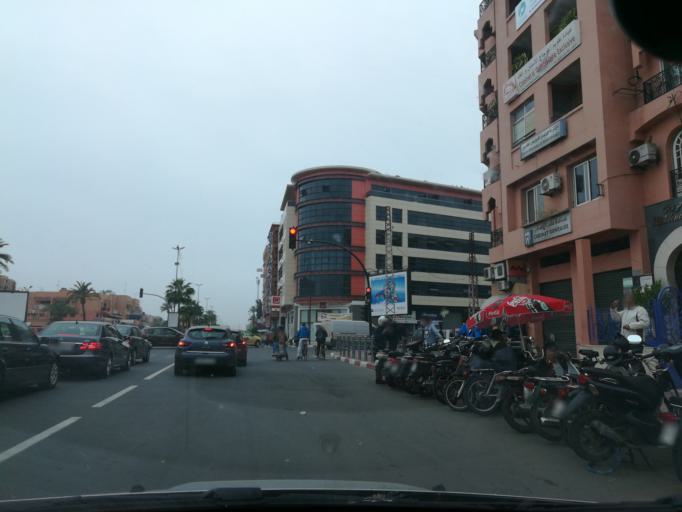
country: MA
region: Marrakech-Tensift-Al Haouz
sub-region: Marrakech
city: Marrakesh
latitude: 31.6402
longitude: -7.9999
